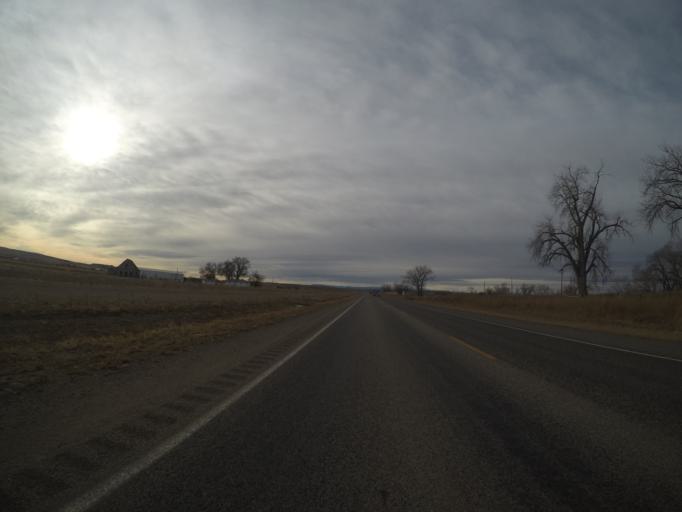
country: US
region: Montana
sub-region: Yellowstone County
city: Laurel
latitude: 45.6203
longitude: -108.8116
